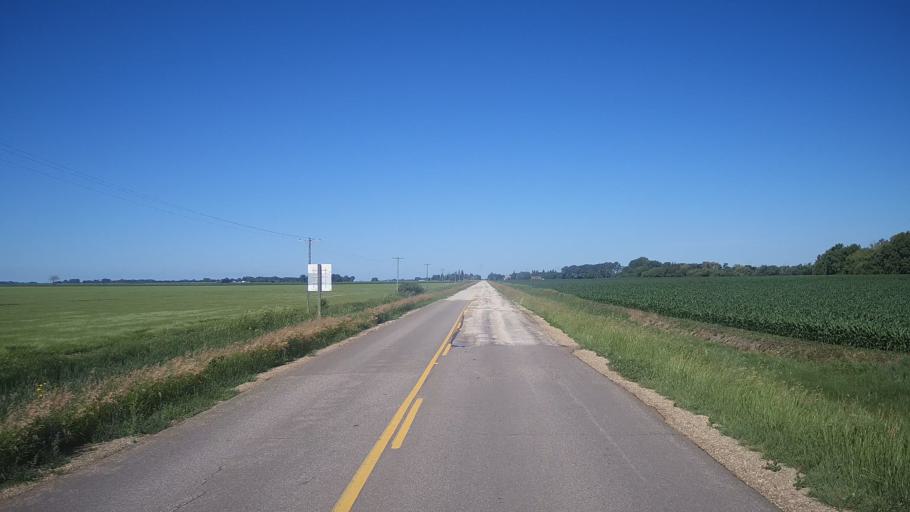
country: CA
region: Manitoba
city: Portage la Prairie
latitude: 50.0435
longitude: -98.0357
